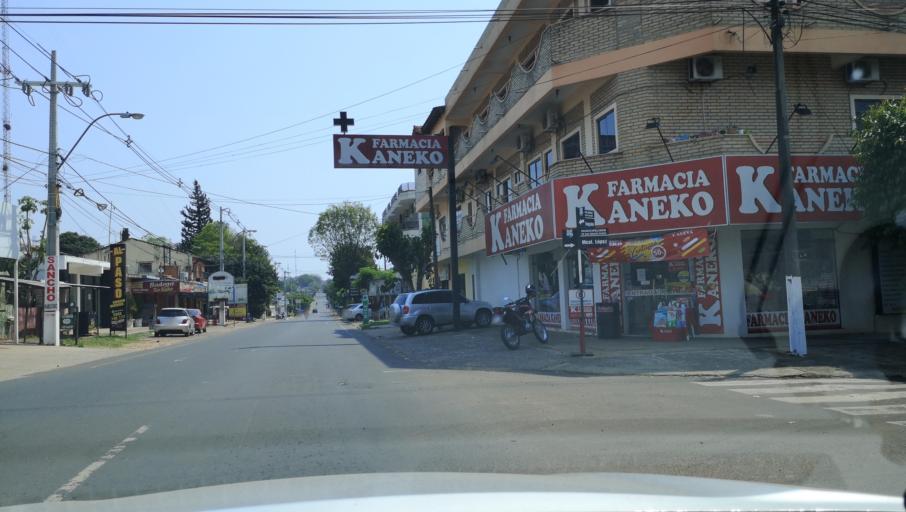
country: PY
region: Misiones
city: Santa Maria
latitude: -26.8857
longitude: -57.0255
